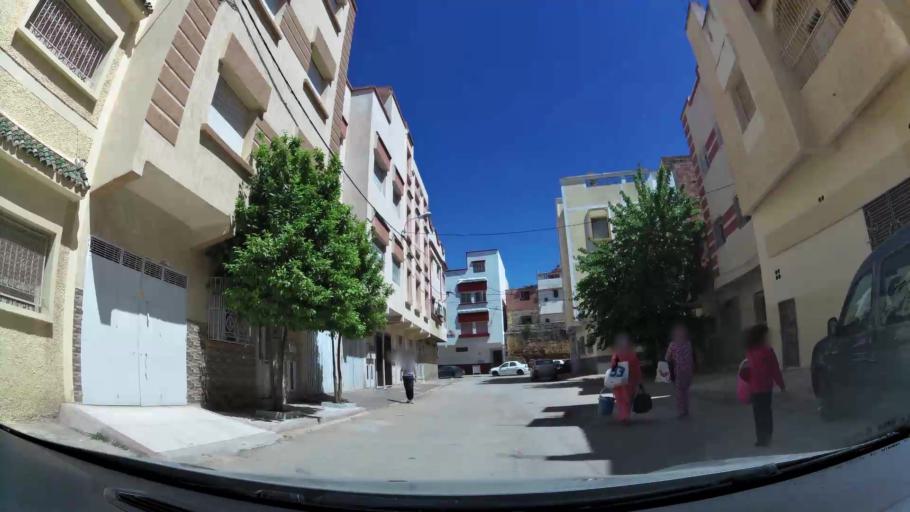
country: MA
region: Meknes-Tafilalet
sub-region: Meknes
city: Meknes
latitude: 33.8725
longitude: -5.5627
